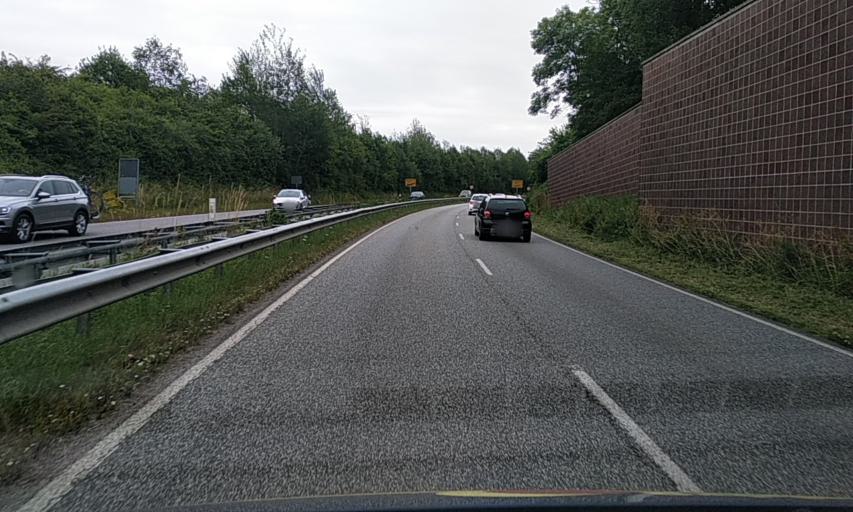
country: DE
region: Schleswig-Holstein
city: Kappeln
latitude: 54.6594
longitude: 9.9423
